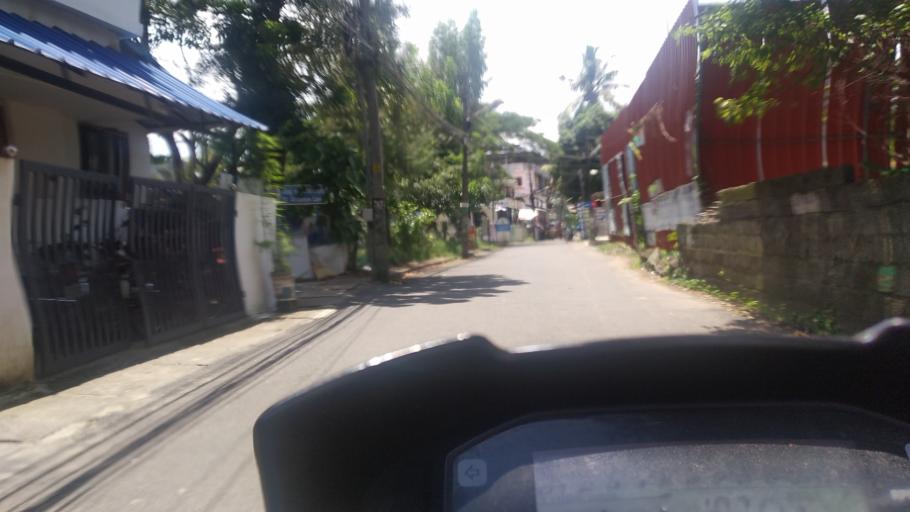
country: IN
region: Kerala
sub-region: Ernakulam
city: Cochin
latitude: 9.9766
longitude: 76.3034
